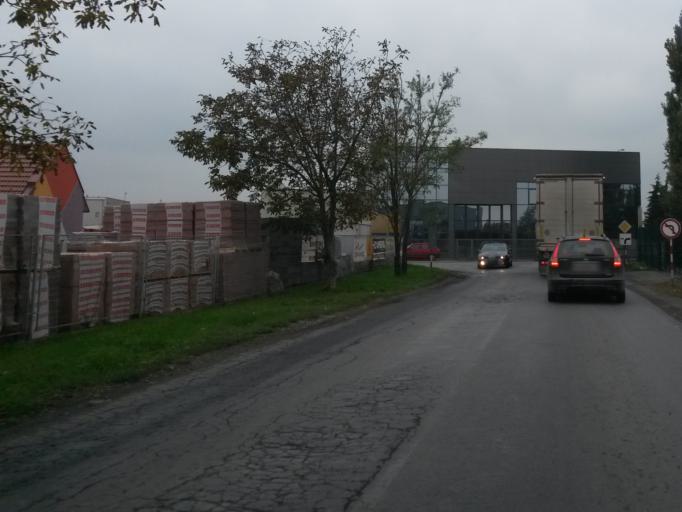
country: HR
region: Osjecko-Baranjska
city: Brijest
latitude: 45.5383
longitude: 18.6463
